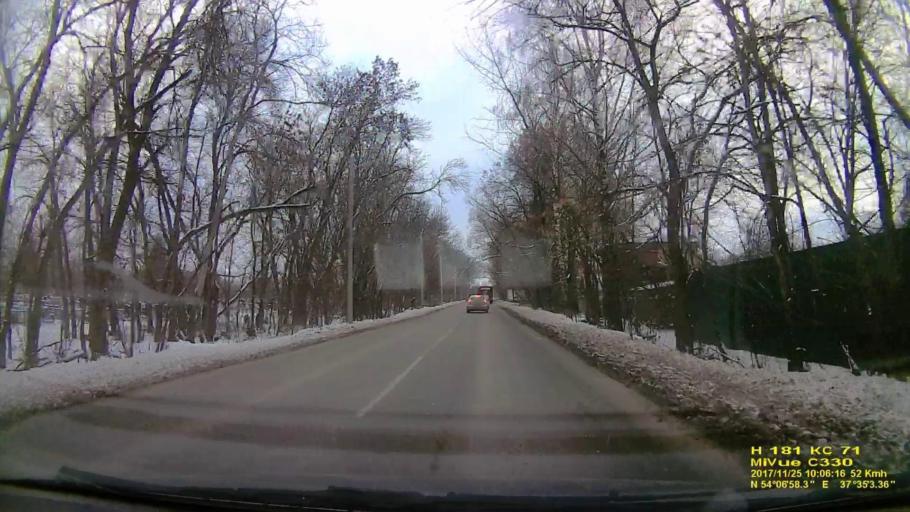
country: RU
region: Tula
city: Mendeleyevskiy
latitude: 54.1161
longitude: 37.5846
